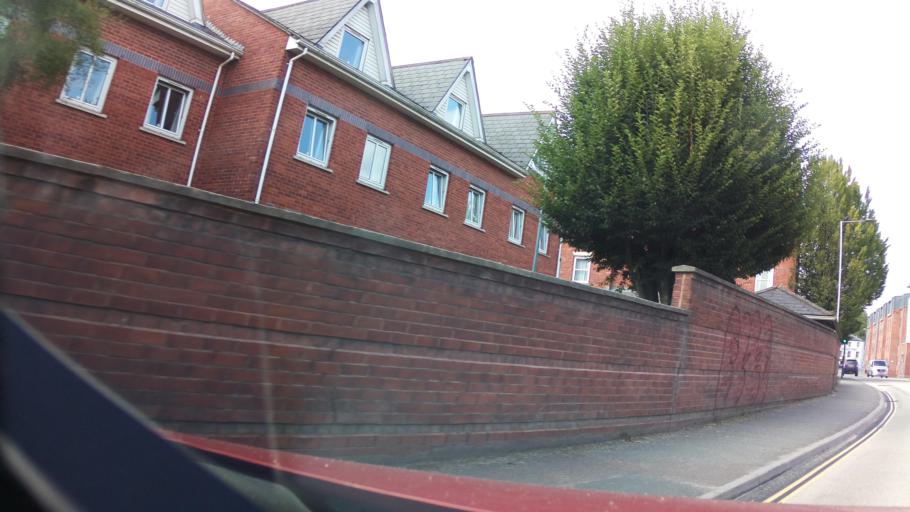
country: GB
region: England
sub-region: Devon
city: Exeter
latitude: 50.7285
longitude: -3.5425
